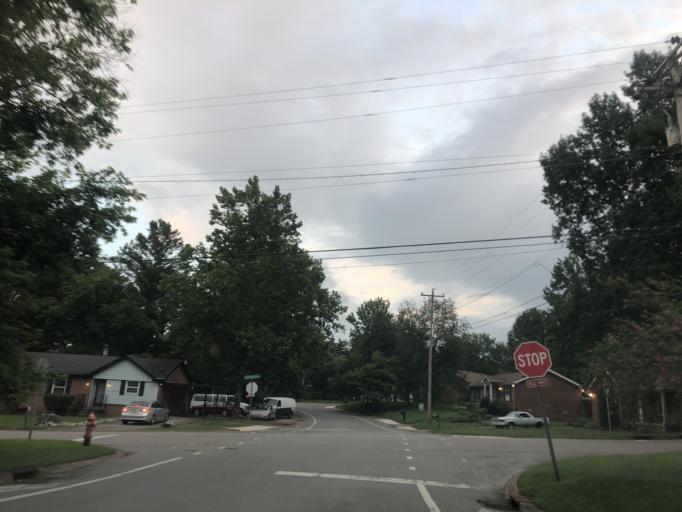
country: US
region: Tennessee
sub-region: Davidson County
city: Lakewood
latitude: 36.1491
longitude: -86.6322
